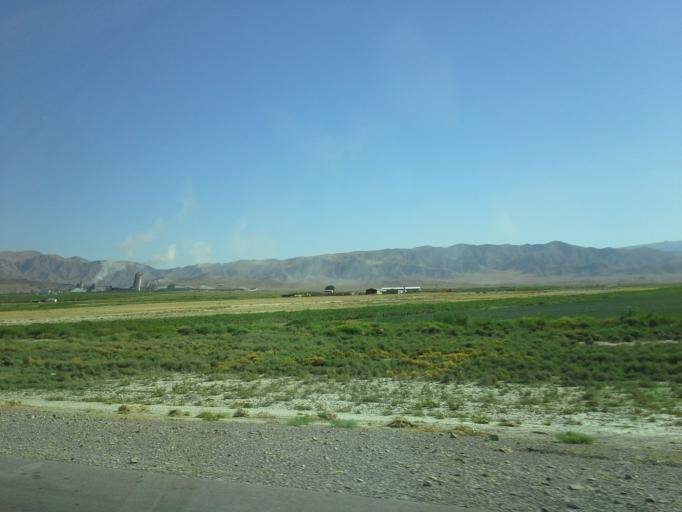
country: TM
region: Ahal
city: Baharly
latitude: 38.2927
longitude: 57.6453
